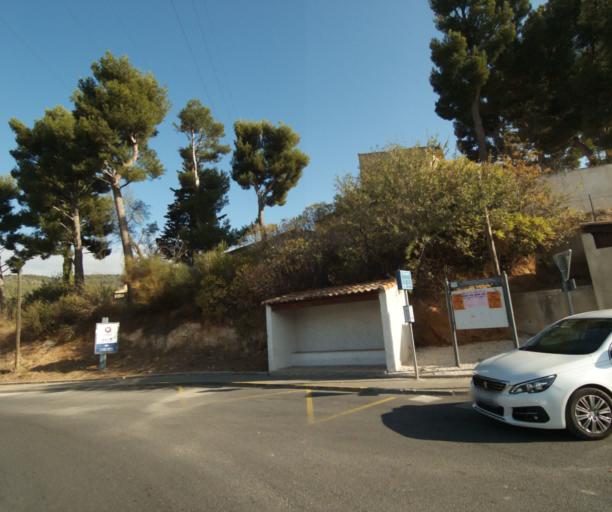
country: FR
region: Provence-Alpes-Cote d'Azur
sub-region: Departement des Bouches-du-Rhone
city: Allauch
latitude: 43.3278
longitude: 5.4906
